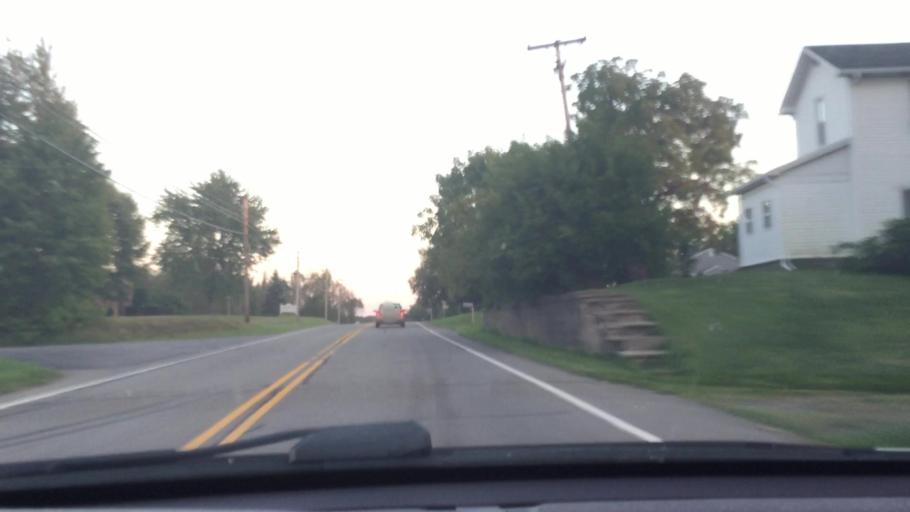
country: US
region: Pennsylvania
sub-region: Mercer County
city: Grove City
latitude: 41.1408
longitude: -80.0794
